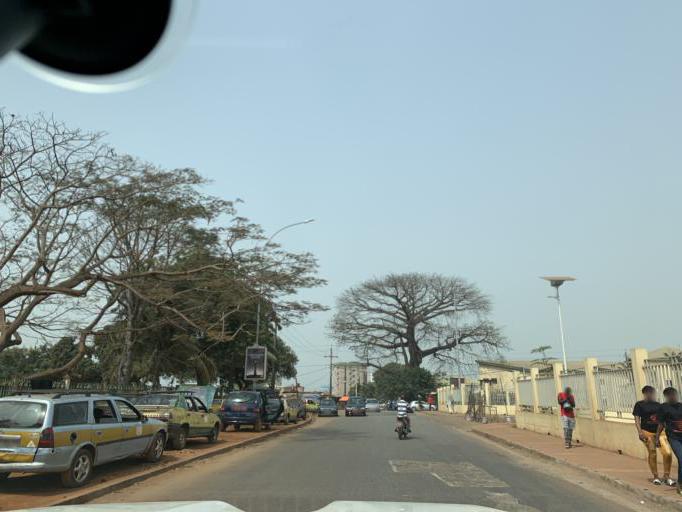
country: GN
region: Conakry
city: Camayenne
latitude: 9.5351
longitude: -13.6844
